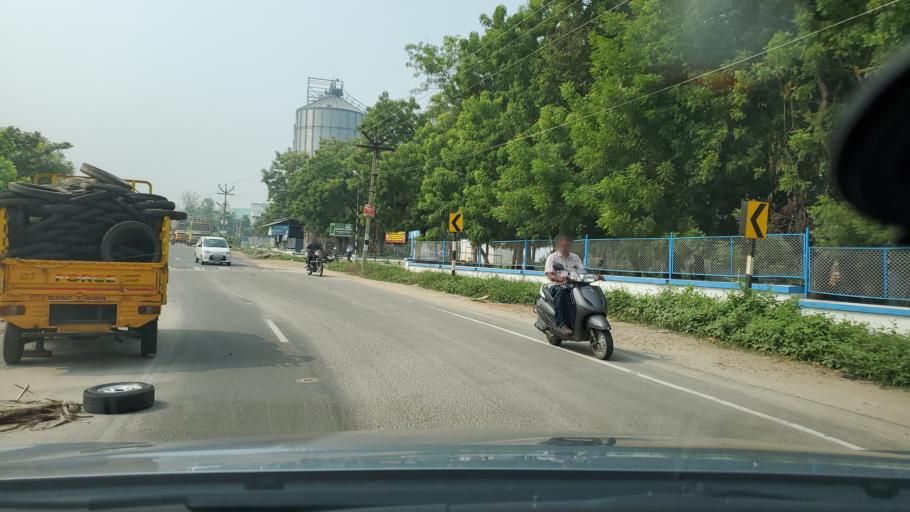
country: IN
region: Tamil Nadu
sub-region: Erode
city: Erode
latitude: 11.3226
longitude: 77.7146
